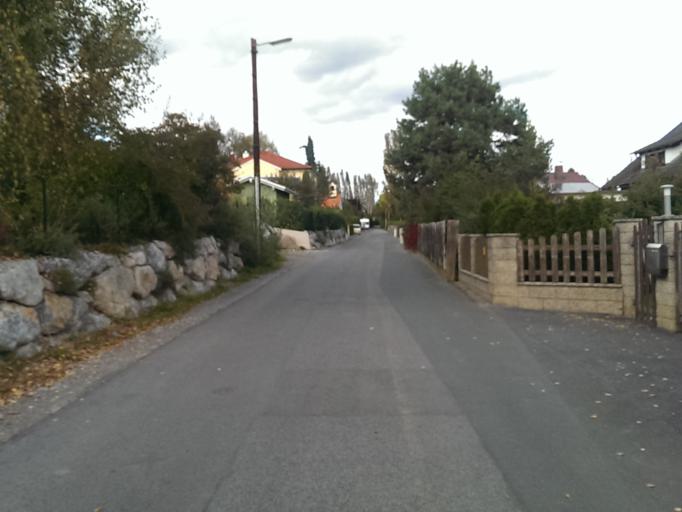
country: AT
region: Styria
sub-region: Graz Stadt
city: Graz
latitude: 47.0648
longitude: 15.4815
